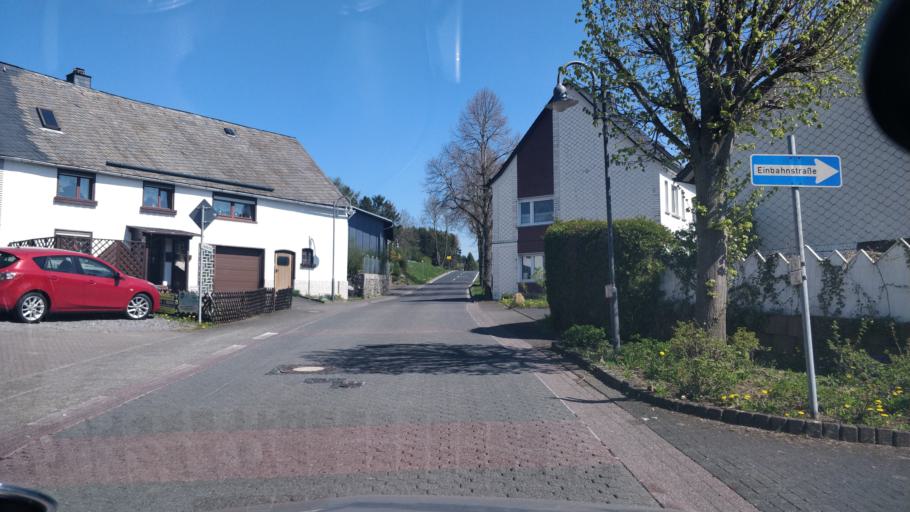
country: DE
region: Rheinland-Pfalz
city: Hellenhahn-Schellenberg
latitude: 50.6144
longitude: 8.0292
